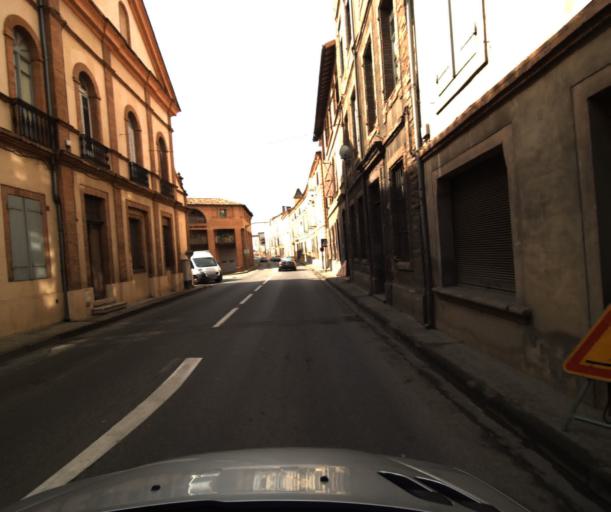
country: FR
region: Midi-Pyrenees
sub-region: Departement du Tarn-et-Garonne
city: Moissac
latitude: 44.1018
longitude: 1.0826
